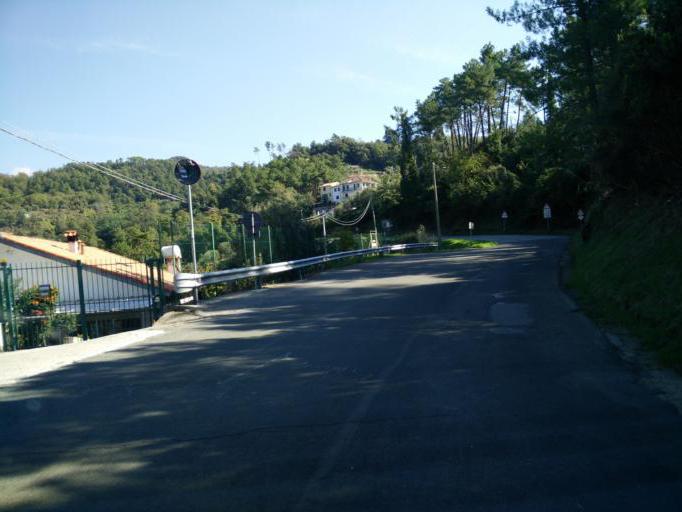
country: IT
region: Liguria
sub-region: Provincia di La Spezia
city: Framura
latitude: 44.2264
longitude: 9.5672
